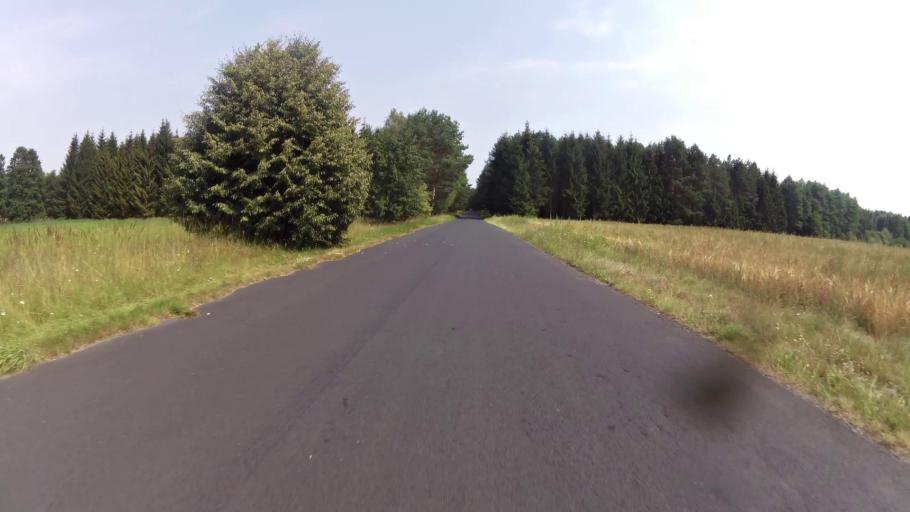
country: PL
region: West Pomeranian Voivodeship
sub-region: Powiat mysliborski
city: Debno
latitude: 52.8452
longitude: 14.7633
